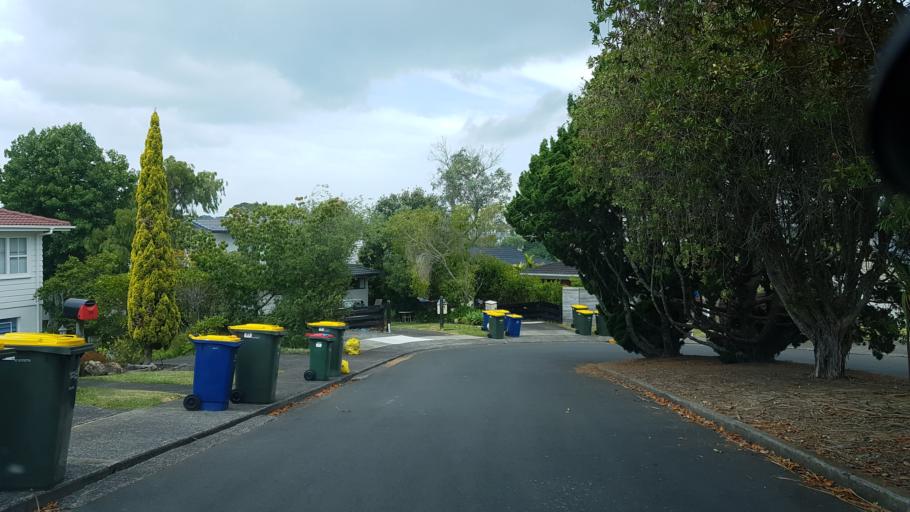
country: NZ
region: Auckland
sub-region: Auckland
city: North Shore
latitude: -36.8038
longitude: 174.7771
